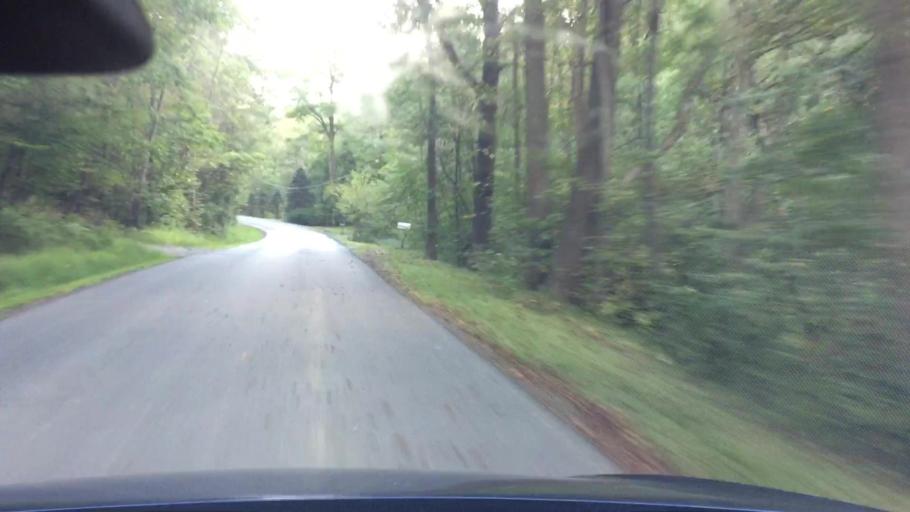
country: US
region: Pennsylvania
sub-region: Butler County
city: Nixon
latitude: 40.7900
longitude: -79.8872
